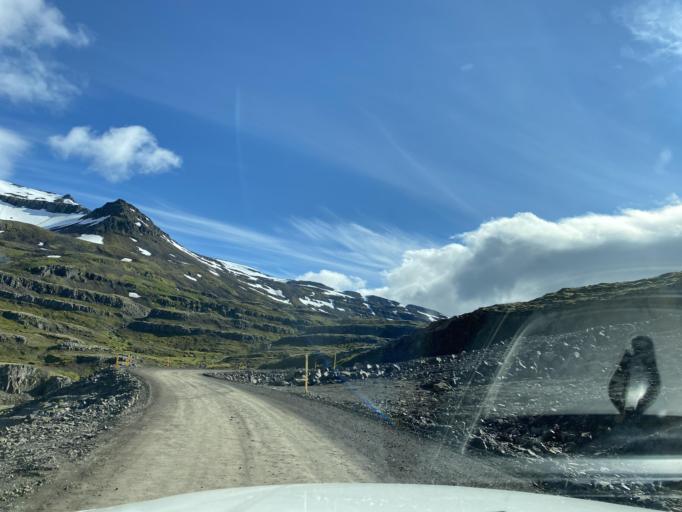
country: IS
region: East
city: Eskifjoerdur
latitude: 65.1781
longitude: -14.0973
